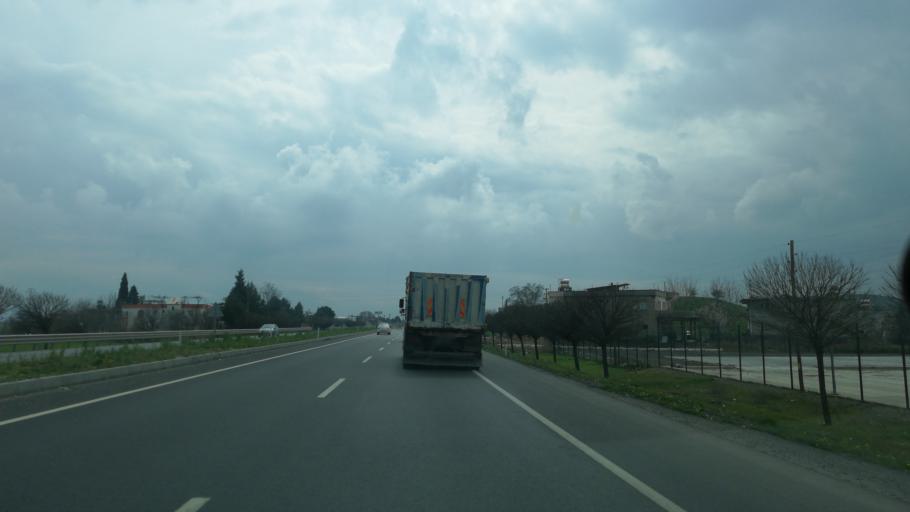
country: TR
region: Kahramanmaras
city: Turkoglu
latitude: 37.4484
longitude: 36.8879
